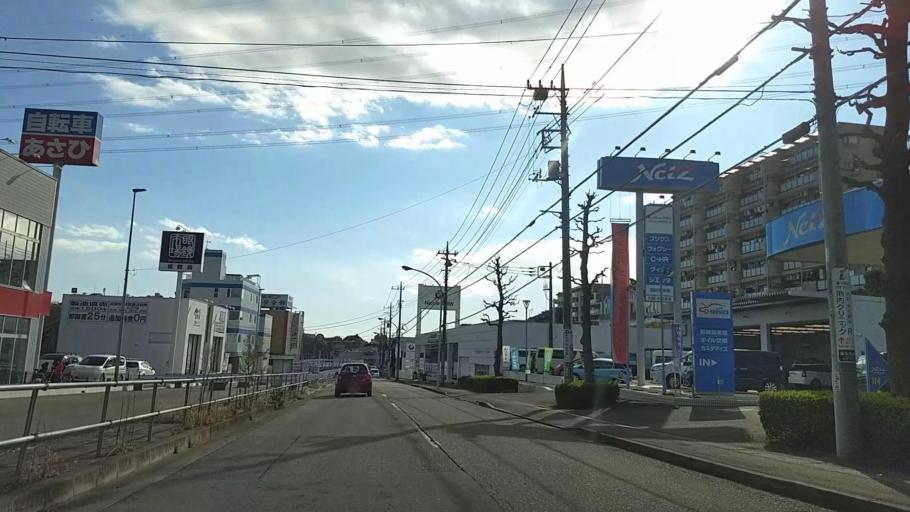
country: JP
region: Tokyo
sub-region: Machida-shi
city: Machida
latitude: 35.5985
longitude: 139.4998
